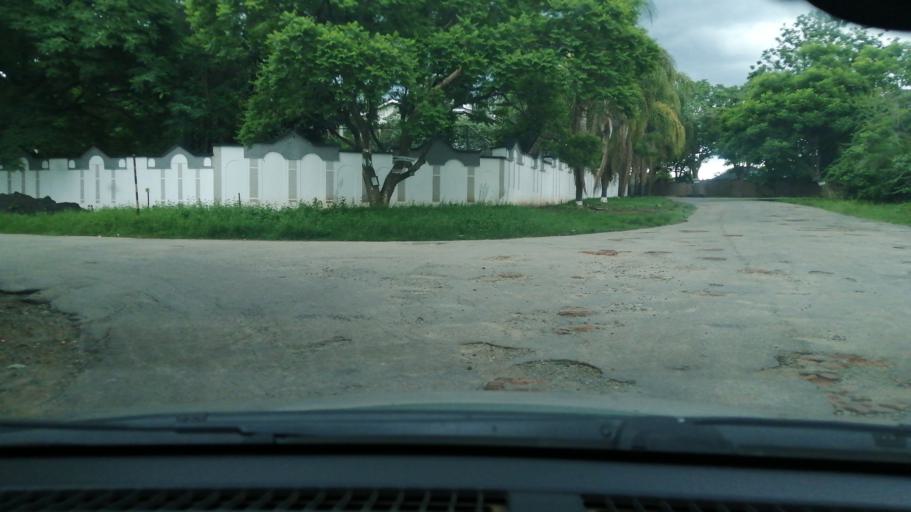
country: ZW
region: Harare
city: Harare
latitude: -17.7735
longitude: 31.0981
